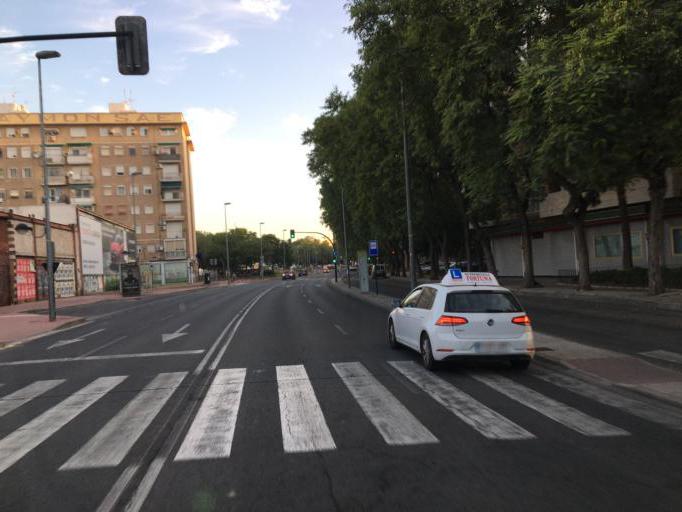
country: ES
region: Murcia
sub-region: Murcia
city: Murcia
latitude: 37.9969
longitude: -1.1428
